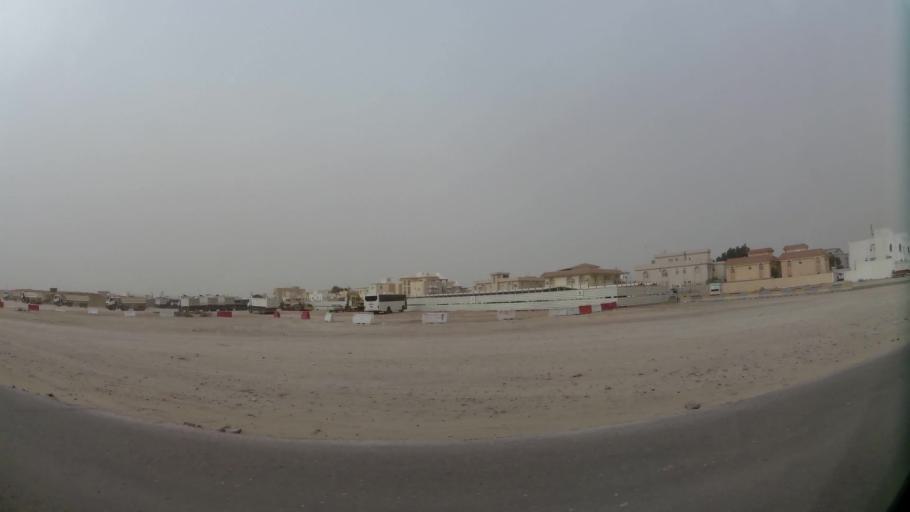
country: QA
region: Baladiyat ad Dawhah
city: Doha
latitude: 25.2522
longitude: 51.4936
